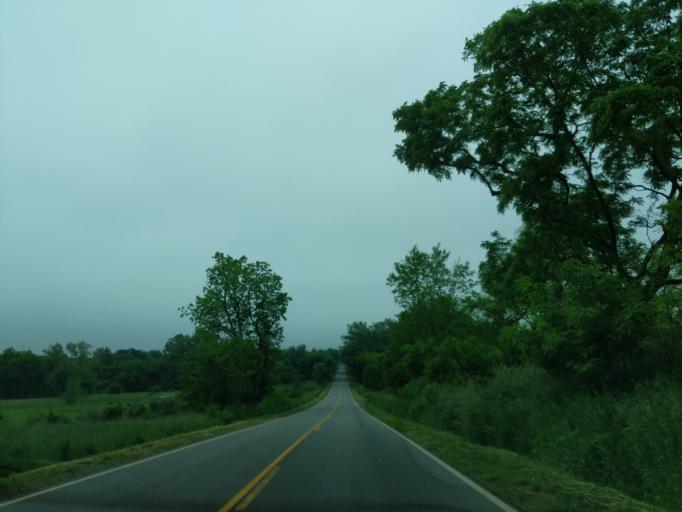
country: US
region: Michigan
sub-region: Jackson County
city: Spring Arbor
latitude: 42.2138
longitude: -84.5703
